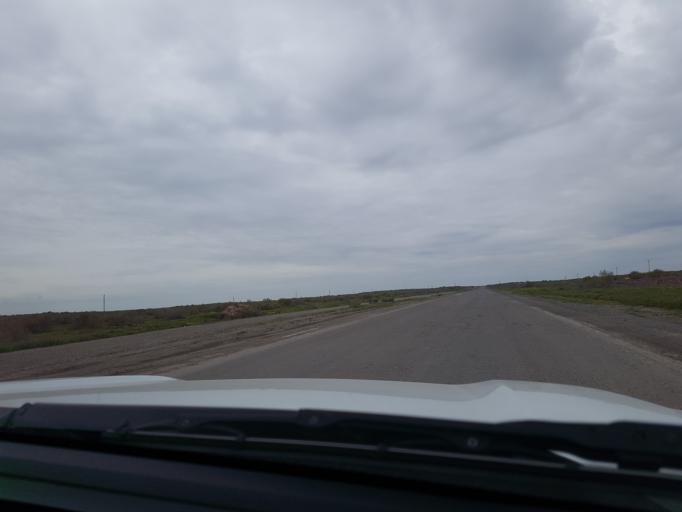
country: TM
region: Mary
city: Bayramaly
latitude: 37.9239
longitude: 62.6245
